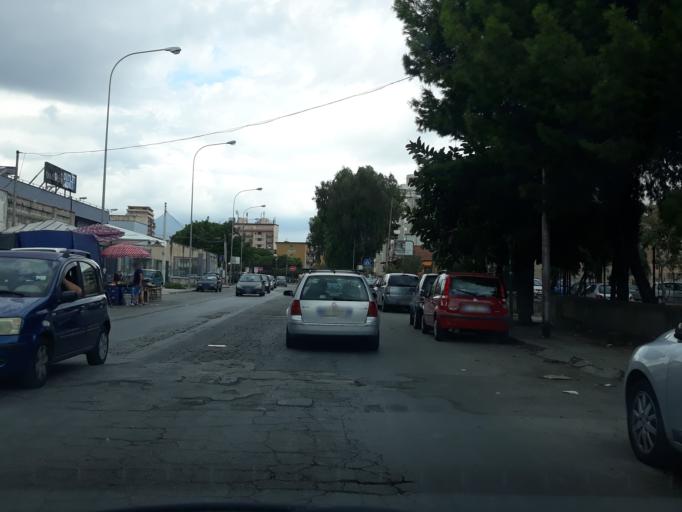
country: IT
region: Sicily
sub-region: Palermo
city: Ciaculli
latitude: 38.0965
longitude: 13.3948
